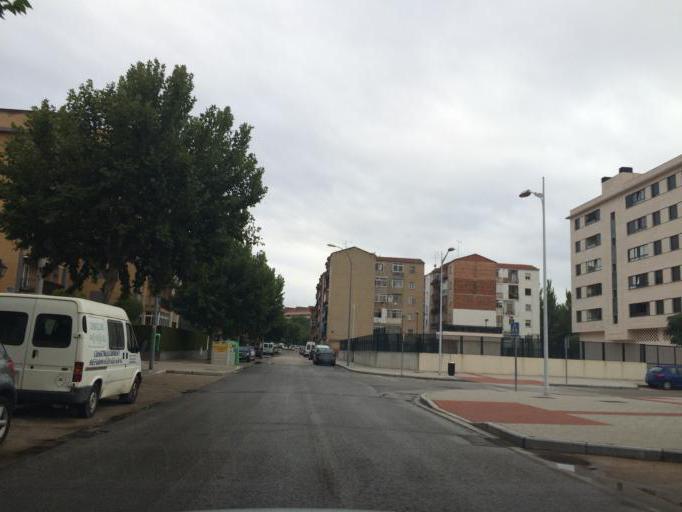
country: ES
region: Castille-La Mancha
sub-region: Provincia de Albacete
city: Albacete
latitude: 39.0047
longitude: -1.8561
